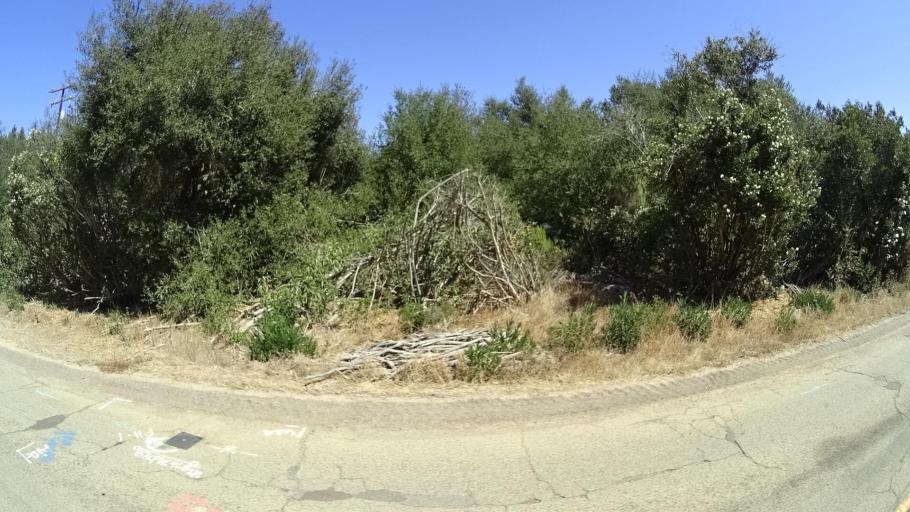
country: US
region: California
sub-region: San Diego County
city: Hidden Meadows
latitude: 33.3152
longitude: -117.0844
